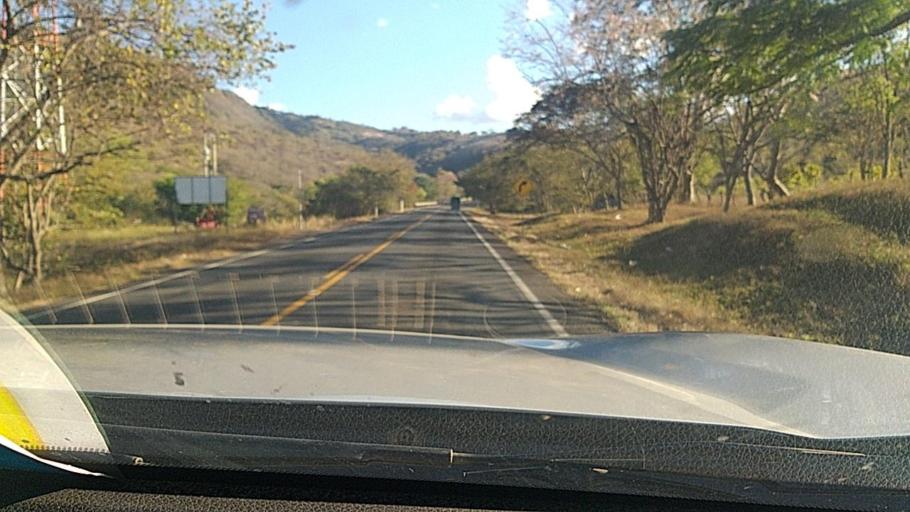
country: NI
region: Esteli
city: Condega
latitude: 13.2858
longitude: -86.3457
